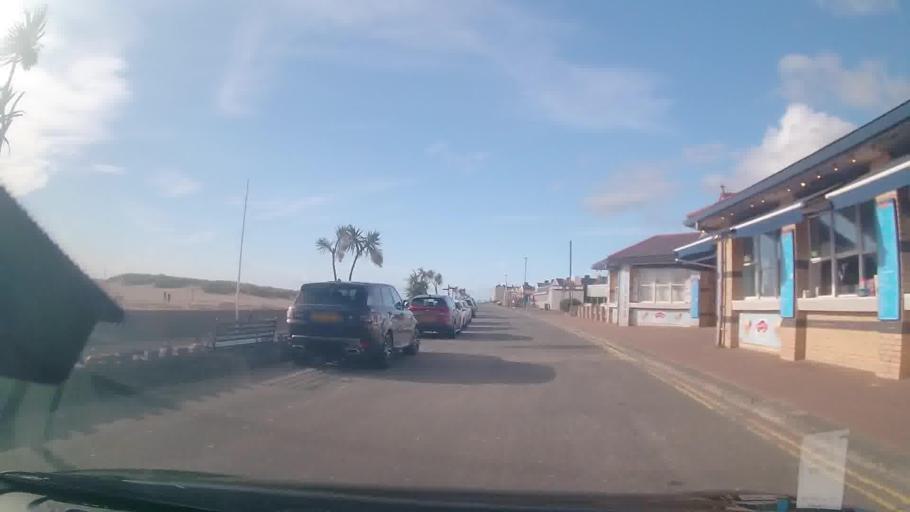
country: GB
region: Wales
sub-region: Gwynedd
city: Barmouth
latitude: 52.7210
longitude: -4.0563
